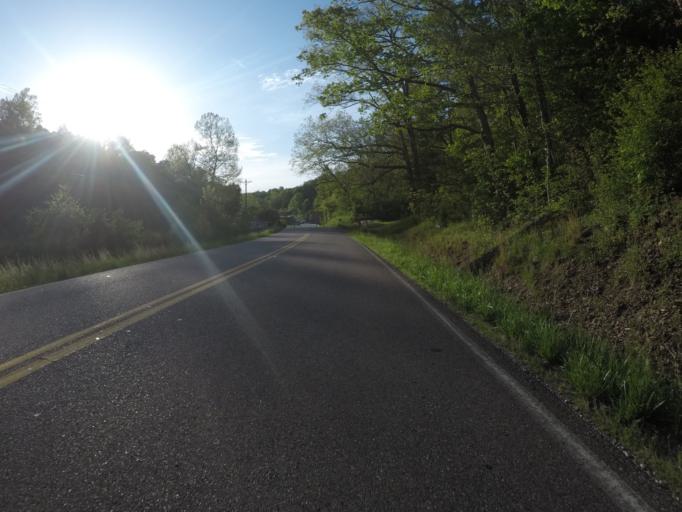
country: US
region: West Virginia
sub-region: Cabell County
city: Huntington
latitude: 38.5522
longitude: -82.4420
